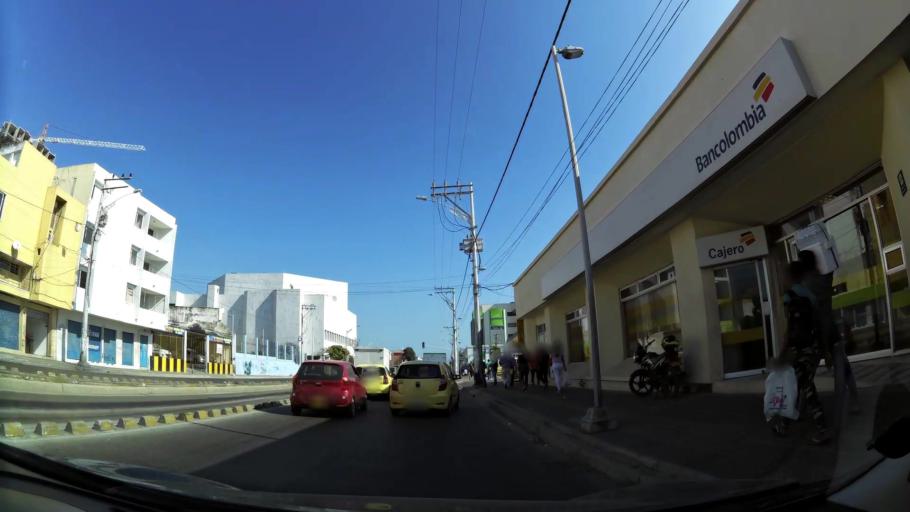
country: CO
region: Atlantico
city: Barranquilla
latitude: 10.9858
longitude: -74.7853
